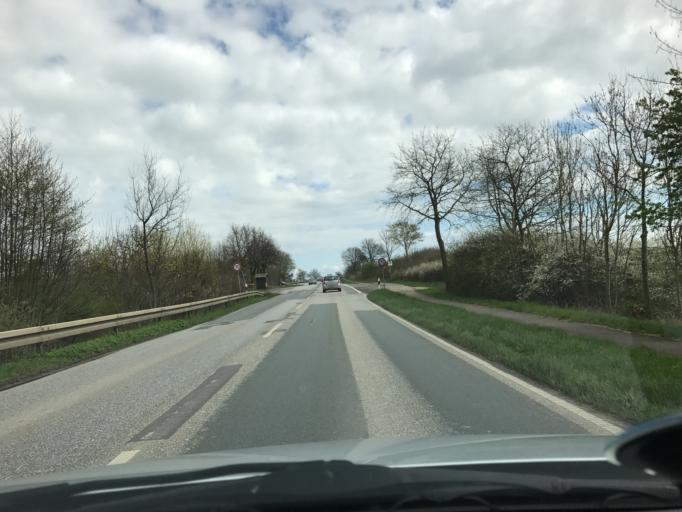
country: DE
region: Schleswig-Holstein
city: Sierksdorf
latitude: 54.0941
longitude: 10.7716
